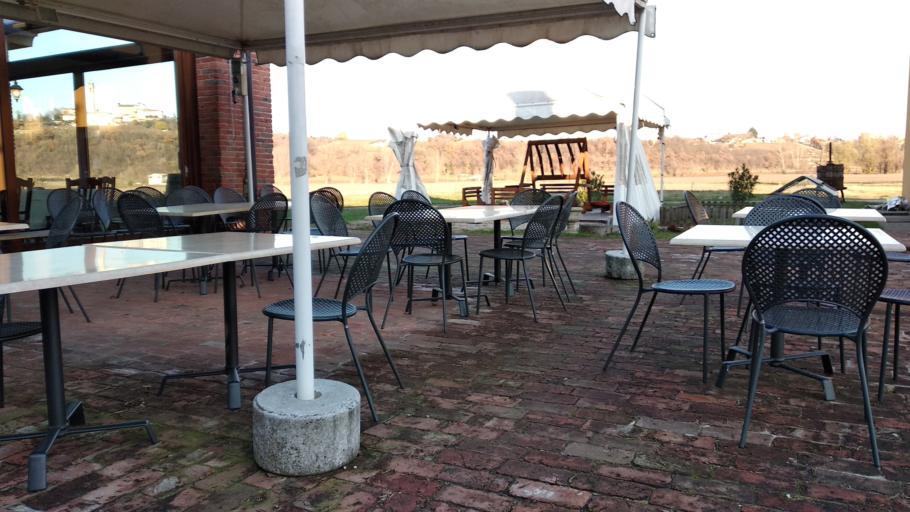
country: IT
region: Veneto
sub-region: Provincia di Vicenza
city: Montecchio Maggiore-Alte Ceccato
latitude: 45.5220
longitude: 11.4182
